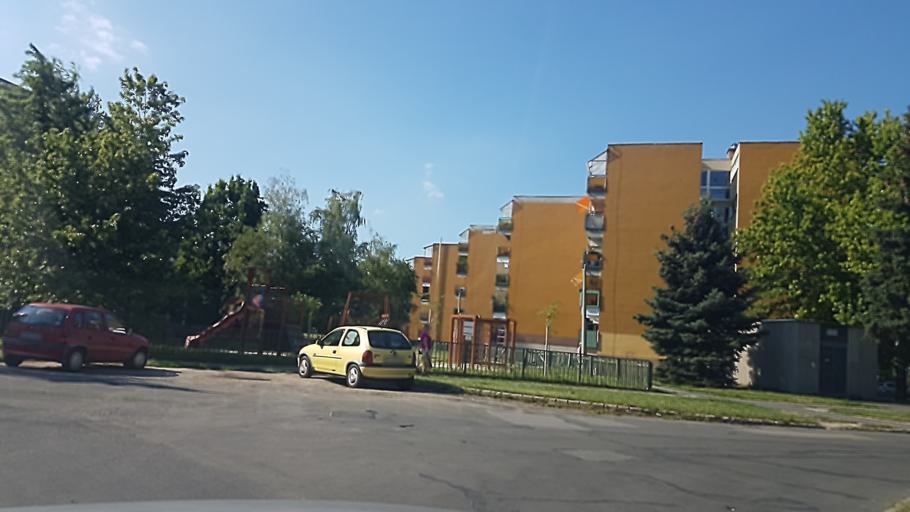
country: HU
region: Gyor-Moson-Sopron
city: Sopron
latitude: 47.6937
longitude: 16.5720
